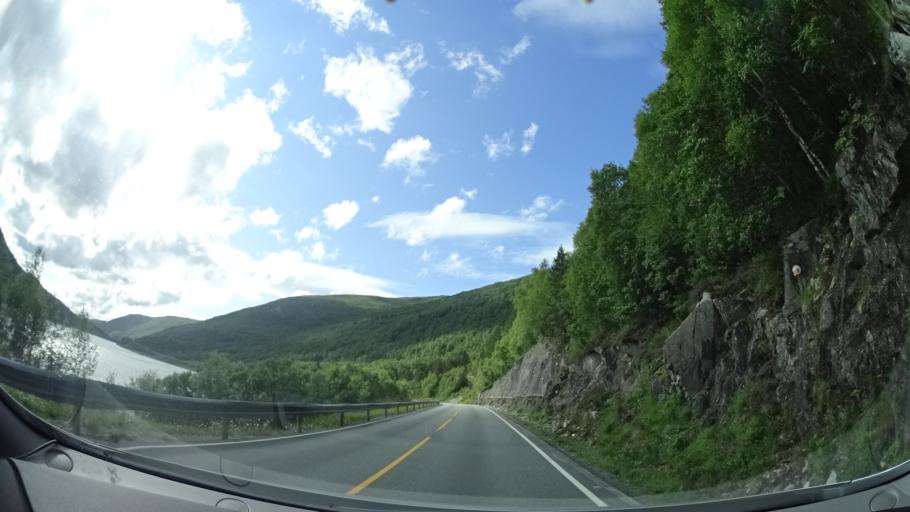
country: NO
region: More og Romsdal
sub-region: Rindal
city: Rindal
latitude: 63.2223
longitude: 9.2587
